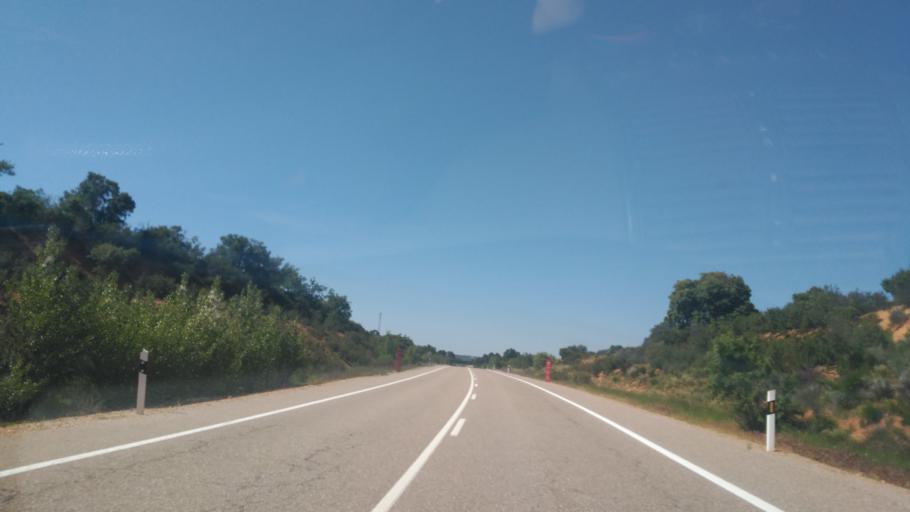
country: ES
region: Castille and Leon
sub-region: Provincia de Zamora
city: Cuelgamures
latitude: 41.2274
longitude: -5.7036
